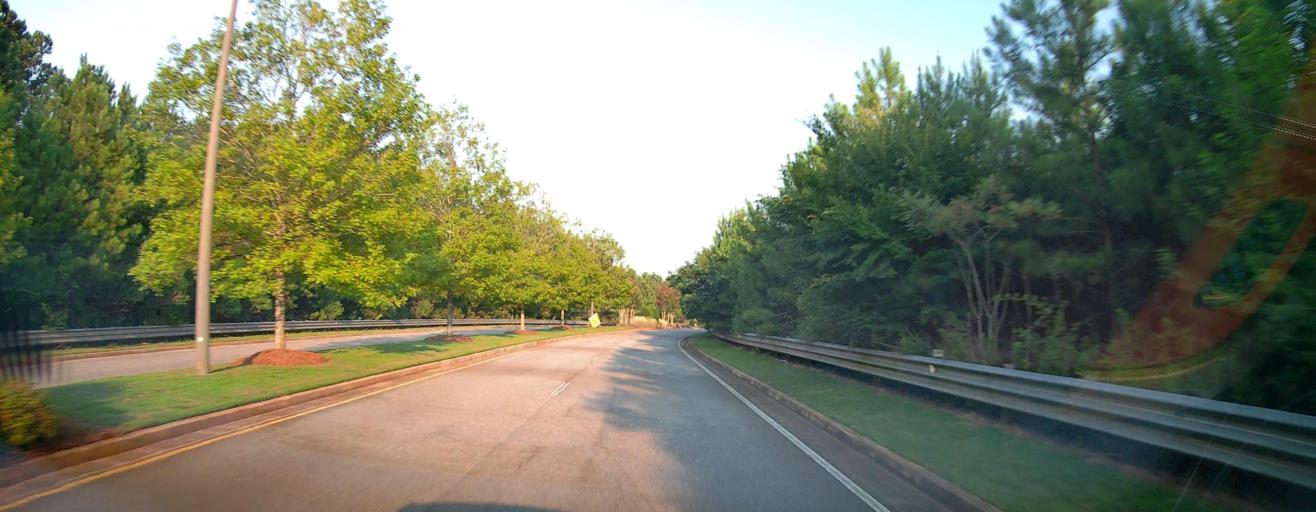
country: US
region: Georgia
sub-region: Bibb County
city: Macon
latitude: 32.9372
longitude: -83.7327
